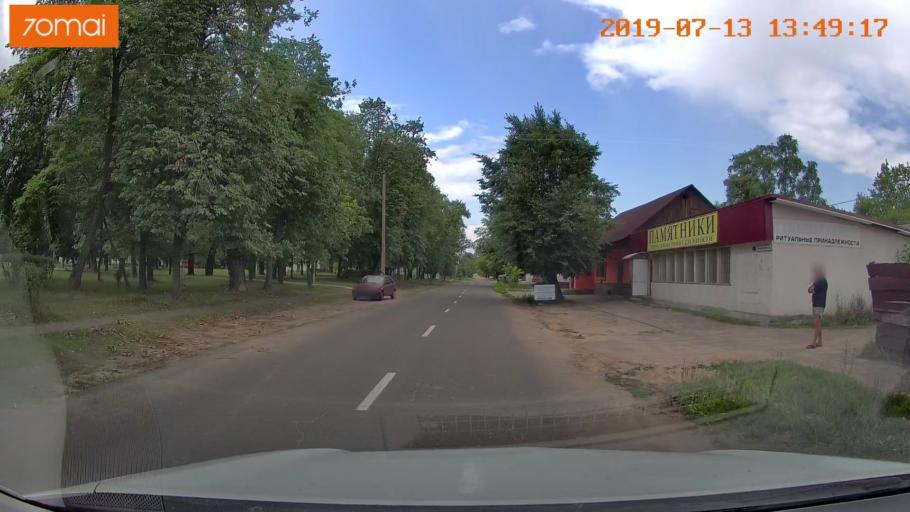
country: BY
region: Mogilev
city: Asipovichy
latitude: 53.2993
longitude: 28.6418
